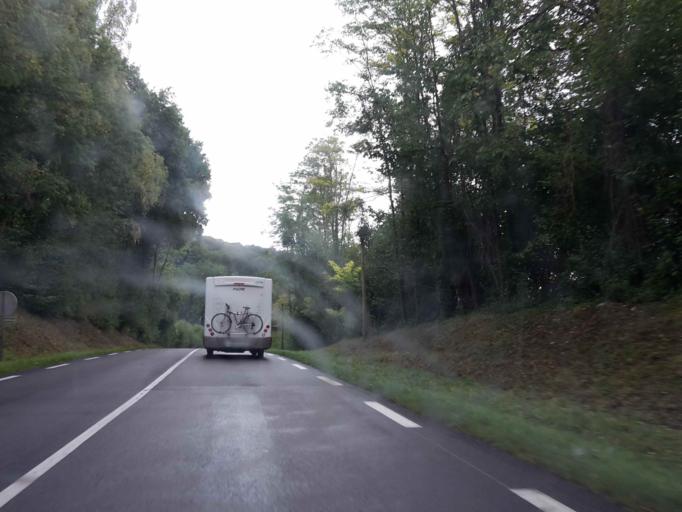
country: FR
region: Franche-Comte
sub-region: Departement du Doubs
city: Roulans
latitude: 47.3070
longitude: 6.1850
